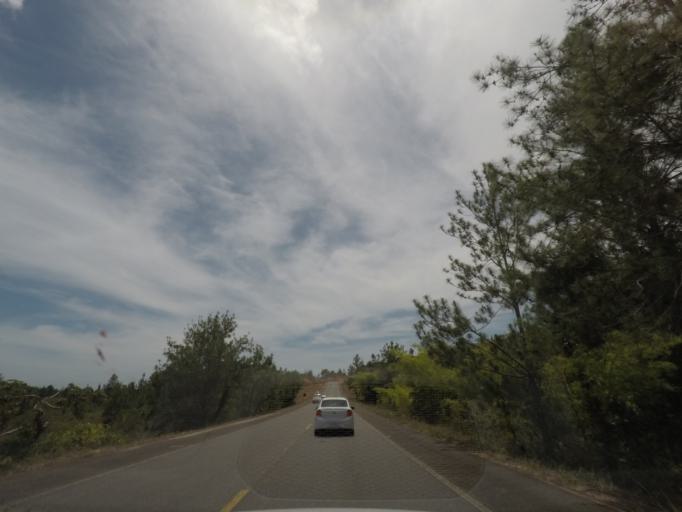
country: BR
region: Bahia
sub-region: Conde
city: Conde
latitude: -11.9905
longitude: -37.6783
